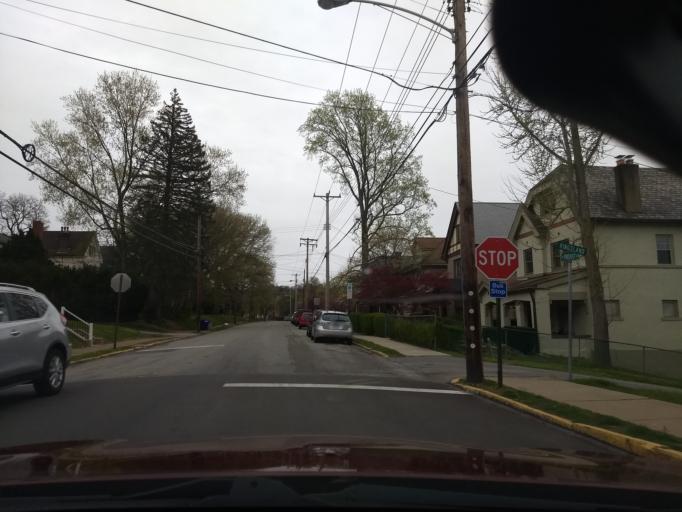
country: US
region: Pennsylvania
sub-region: Allegheny County
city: Ingram
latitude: 40.4476
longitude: -80.0717
